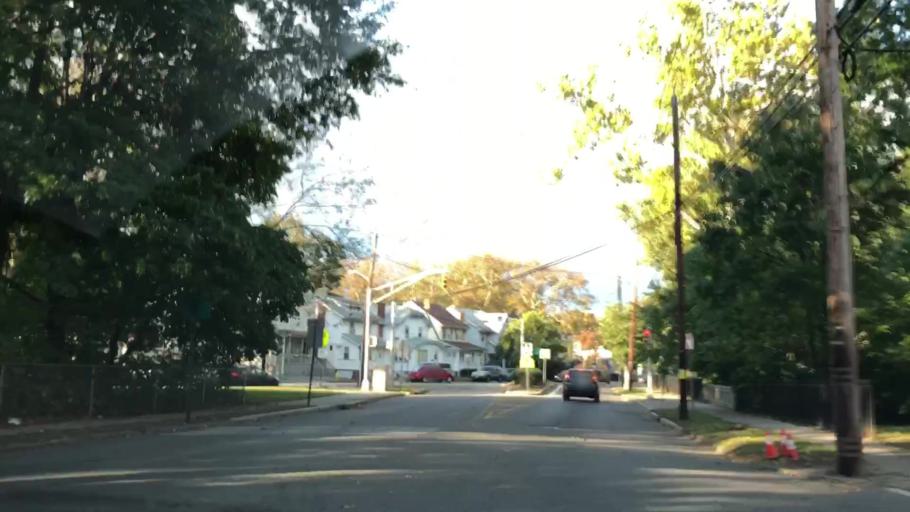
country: US
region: New Jersey
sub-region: Essex County
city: East Orange
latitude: 40.7862
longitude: -74.2040
